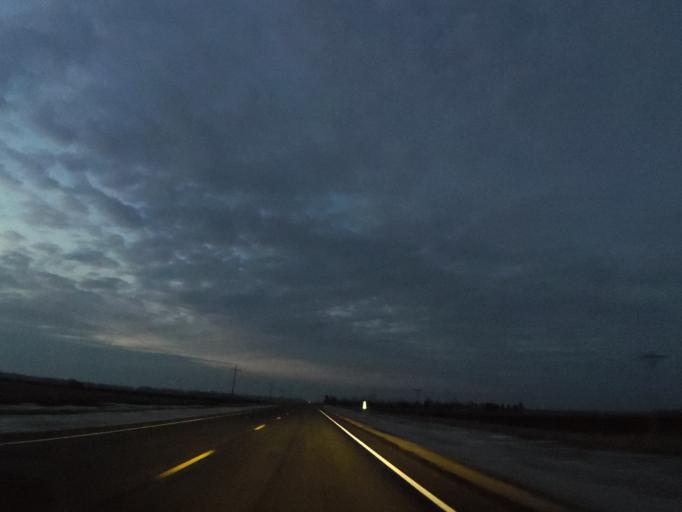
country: US
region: North Dakota
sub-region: Walsh County
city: Park River
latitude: 48.2753
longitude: -97.6224
